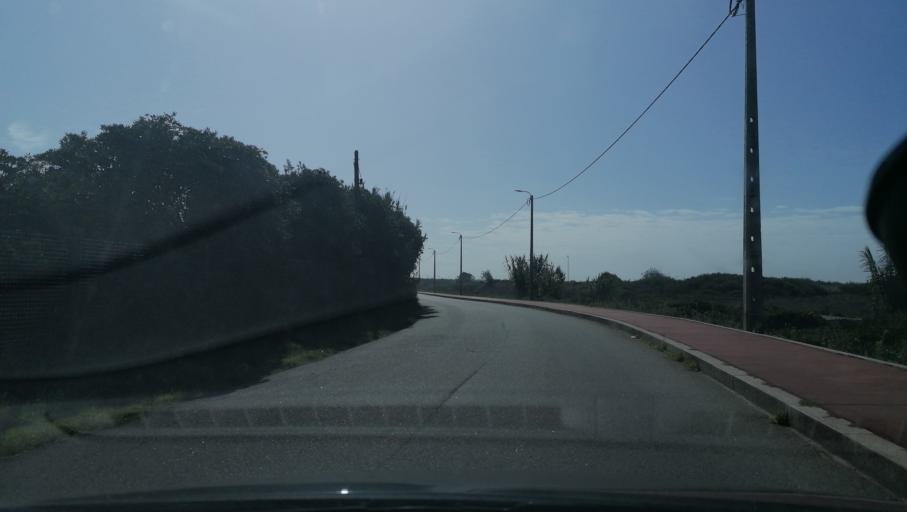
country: PT
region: Aveiro
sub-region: Espinho
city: Silvalde
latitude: 40.9871
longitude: -8.6442
